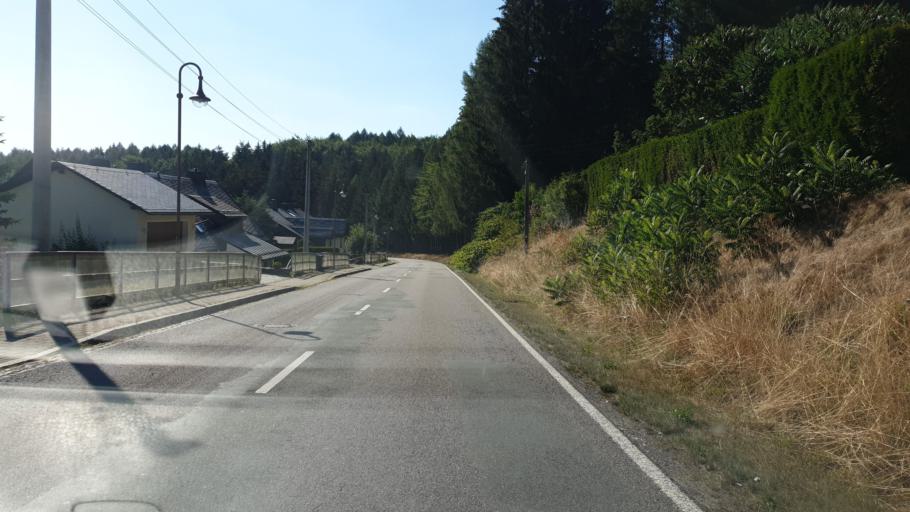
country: DE
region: Saxony
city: Bernsbach
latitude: 50.5895
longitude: 12.7466
